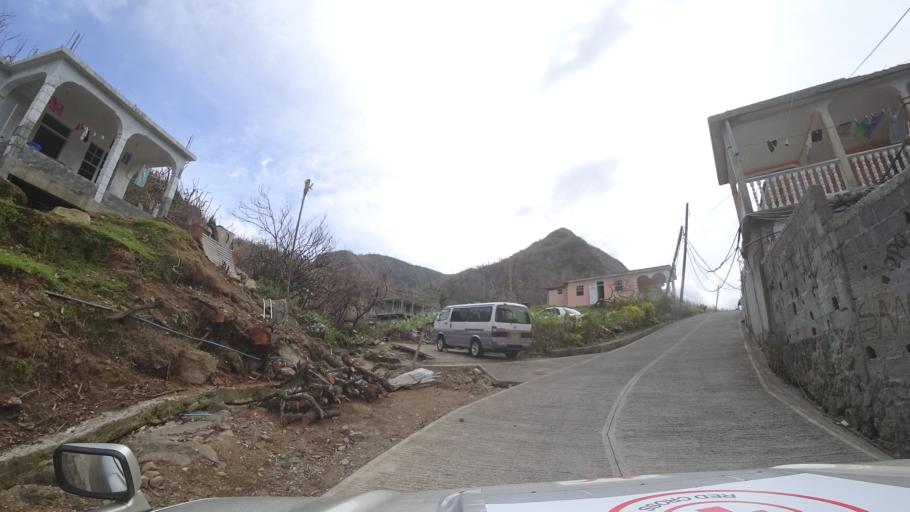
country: DM
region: Saint Patrick
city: Berekua
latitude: 15.2358
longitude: -61.3309
